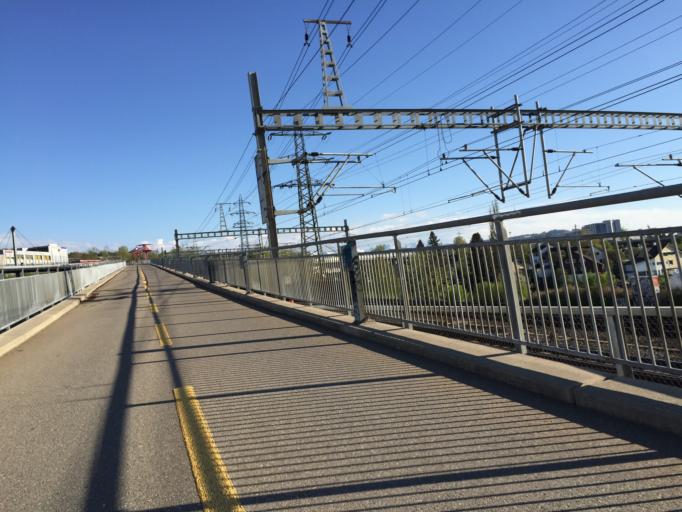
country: CH
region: Bern
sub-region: Bern-Mittelland District
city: Bolligen
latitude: 46.9743
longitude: 7.4699
